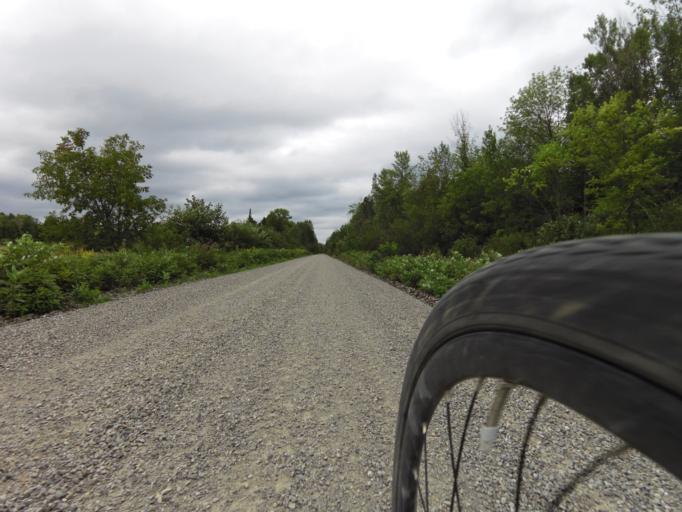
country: CA
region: Ontario
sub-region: Lanark County
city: Smiths Falls
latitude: 44.9572
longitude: -76.0482
